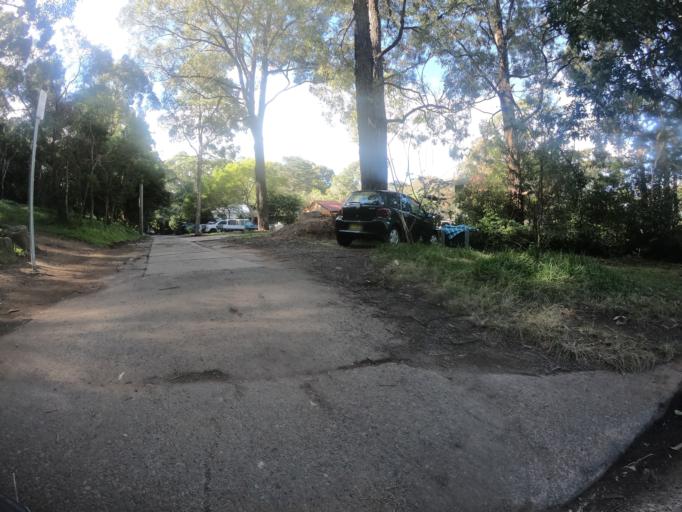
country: AU
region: New South Wales
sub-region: Wollongong
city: Bulli
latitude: -34.3029
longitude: 150.9257
